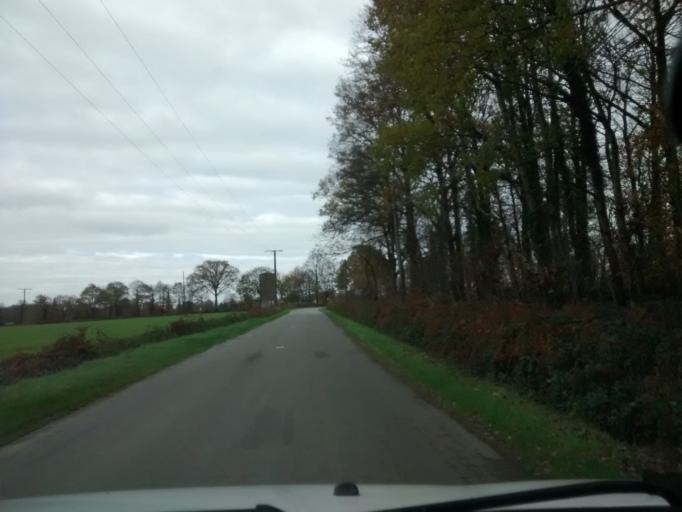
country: FR
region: Brittany
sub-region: Departement d'Ille-et-Vilaine
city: Erbree
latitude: 48.0897
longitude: -1.1498
